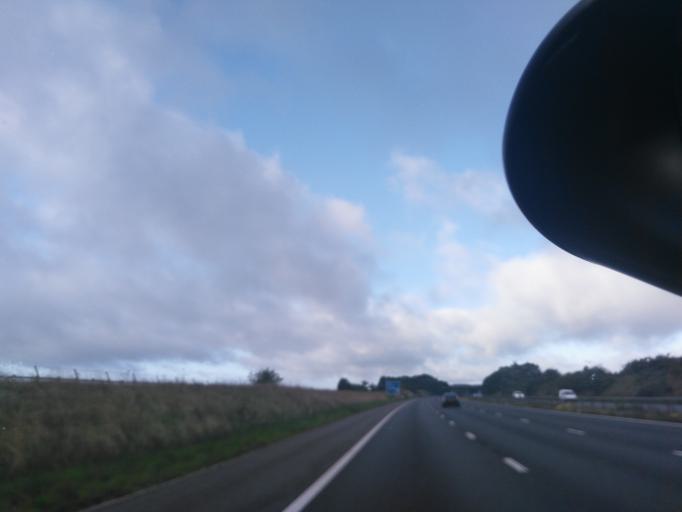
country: GB
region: England
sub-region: South Gloucestershire
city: Marshfield
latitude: 51.5036
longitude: -2.3235
